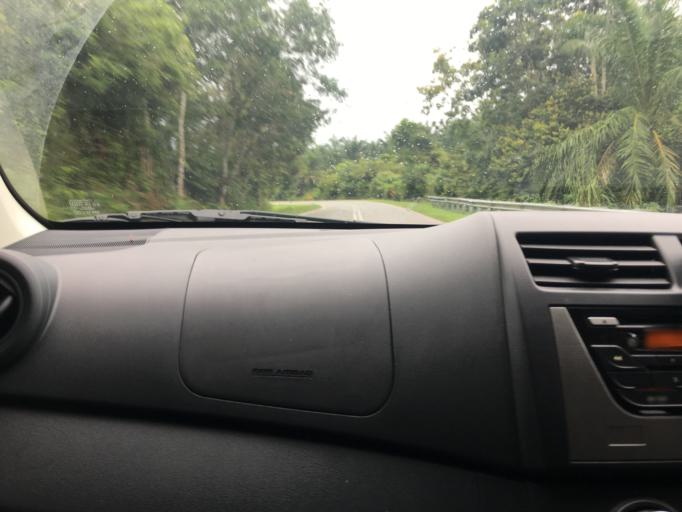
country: MY
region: Kedah
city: Bedong
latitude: 5.7094
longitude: 100.6320
